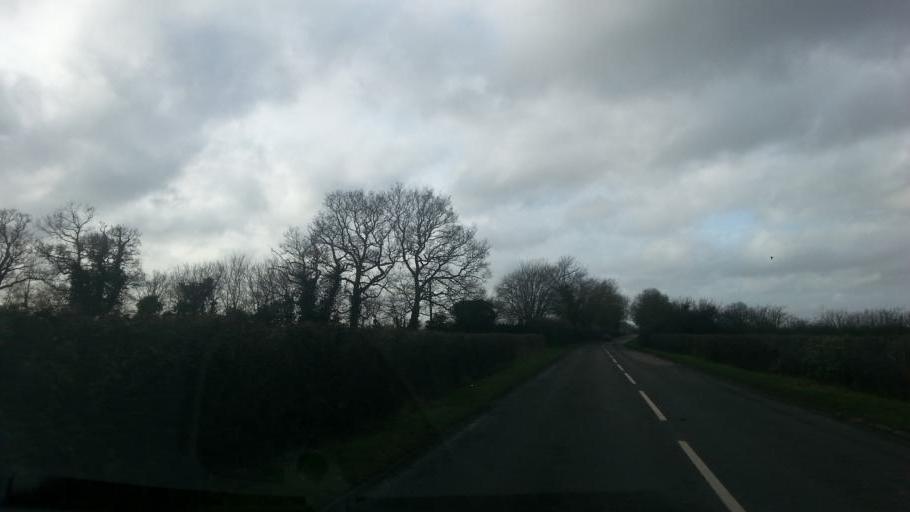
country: GB
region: England
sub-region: District of Rutland
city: Edith Weston
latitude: 52.6359
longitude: -0.6437
